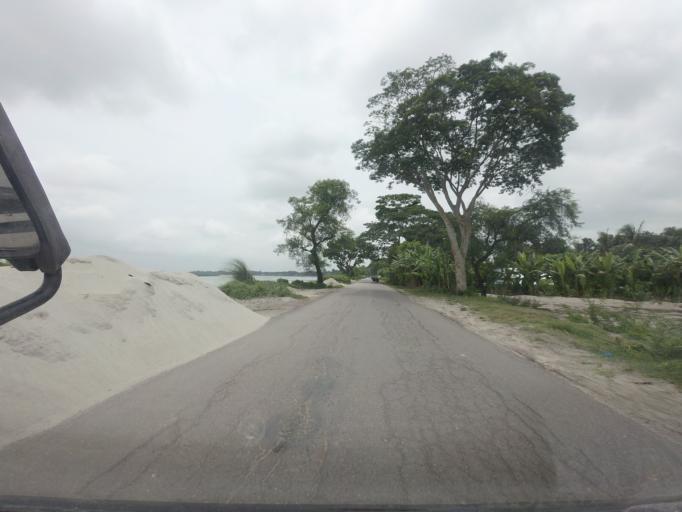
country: BD
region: Khulna
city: Kalia
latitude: 23.2021
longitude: 89.6979
